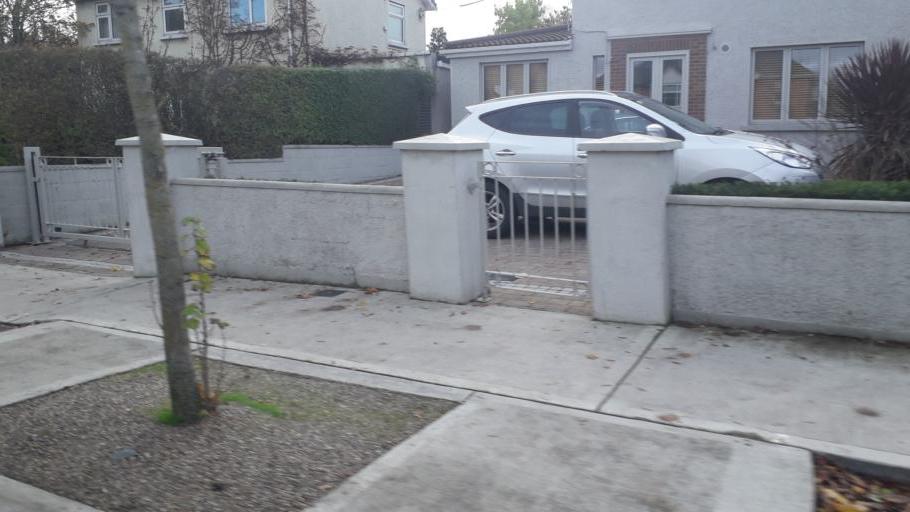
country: IE
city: Milltown
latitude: 53.3052
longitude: -6.2385
